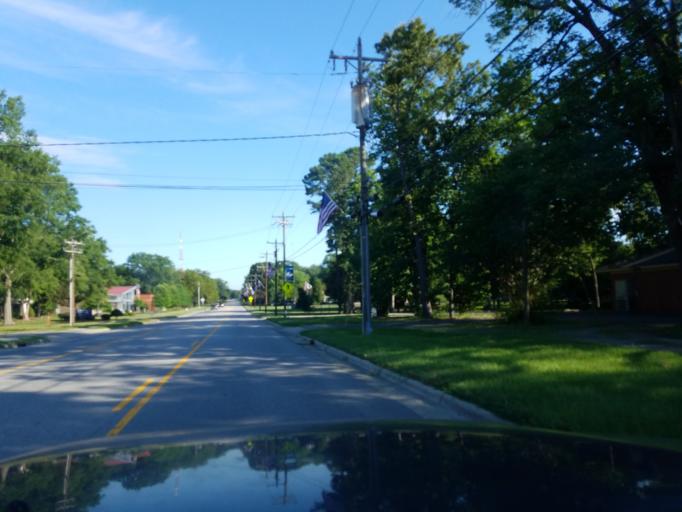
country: US
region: North Carolina
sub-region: Granville County
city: Butner
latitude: 36.1357
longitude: -78.7600
